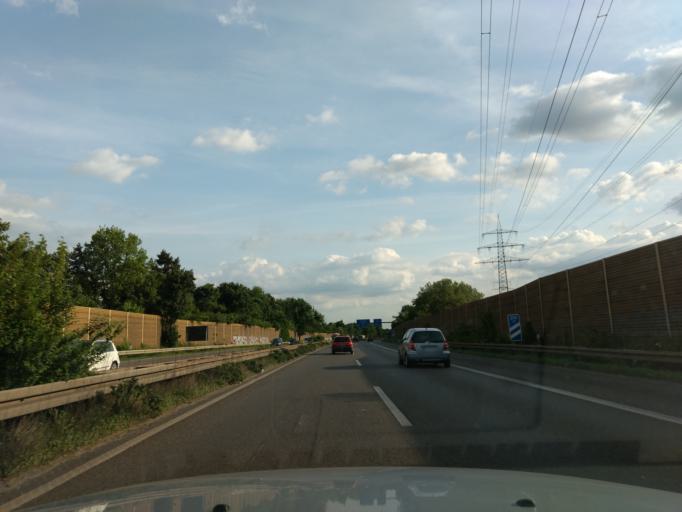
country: DE
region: North Rhine-Westphalia
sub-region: Regierungsbezirk Dusseldorf
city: Neuss
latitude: 51.1863
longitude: 6.7134
